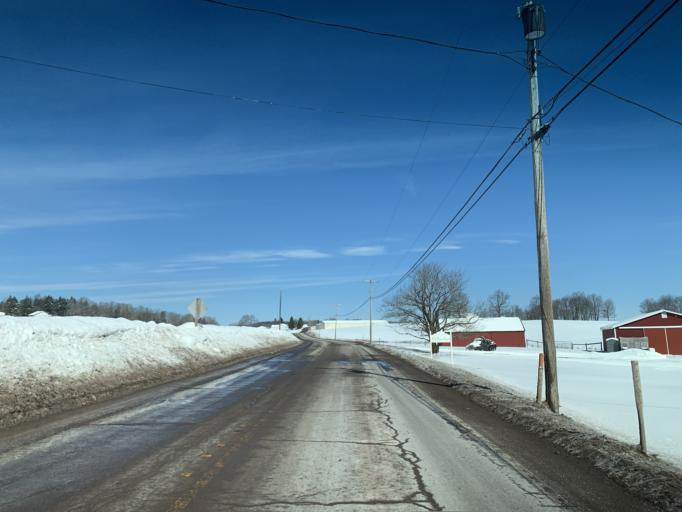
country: US
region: Pennsylvania
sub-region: Somerset County
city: Meyersdale
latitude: 39.7047
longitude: -79.1609
